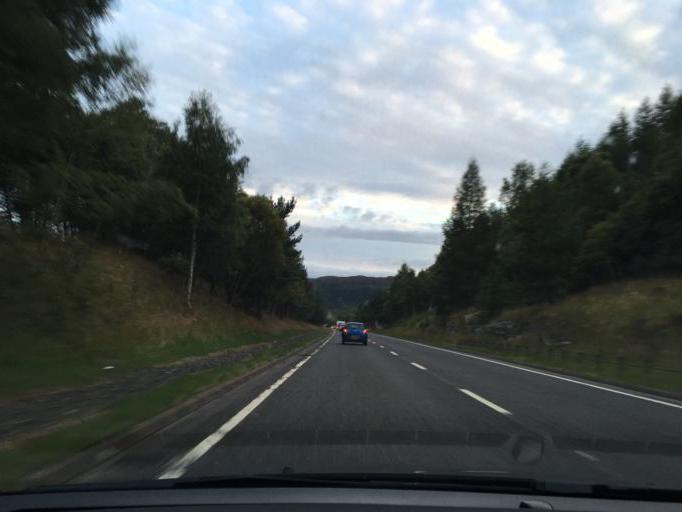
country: GB
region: Scotland
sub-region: Highland
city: Aviemore
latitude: 57.2080
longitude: -3.8296
